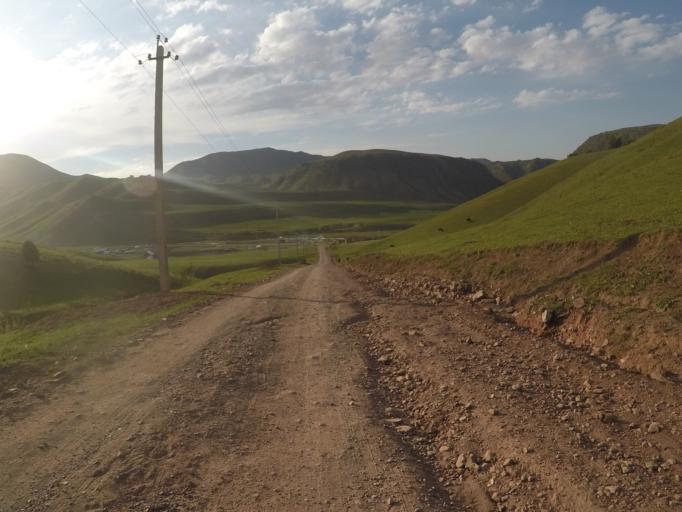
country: KG
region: Chuy
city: Bishkek
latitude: 42.6317
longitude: 74.6181
